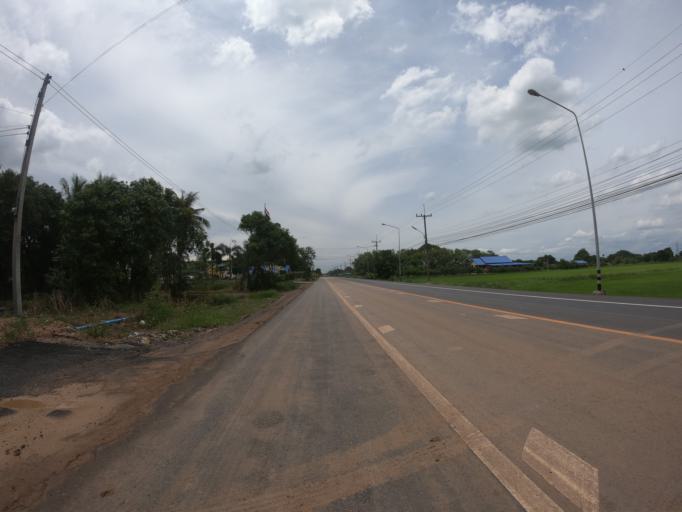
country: TH
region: Pathum Thani
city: Ban Lam Luk Ka
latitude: 14.0354
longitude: 100.8699
